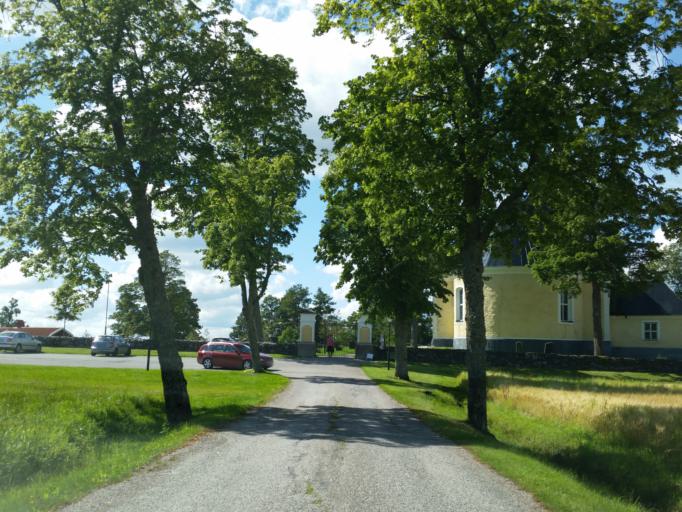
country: SE
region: Soedermanland
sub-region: Trosa Kommun
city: Vagnharad
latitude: 59.0134
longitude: 17.5910
